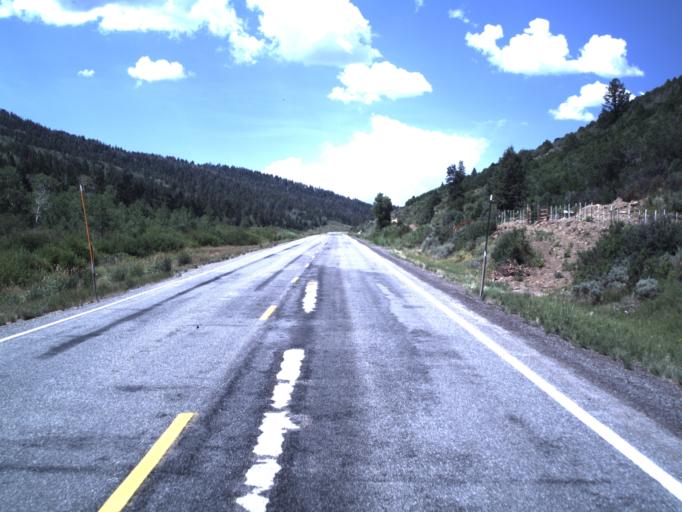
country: US
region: Utah
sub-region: Carbon County
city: Helper
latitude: 39.8567
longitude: -111.0727
